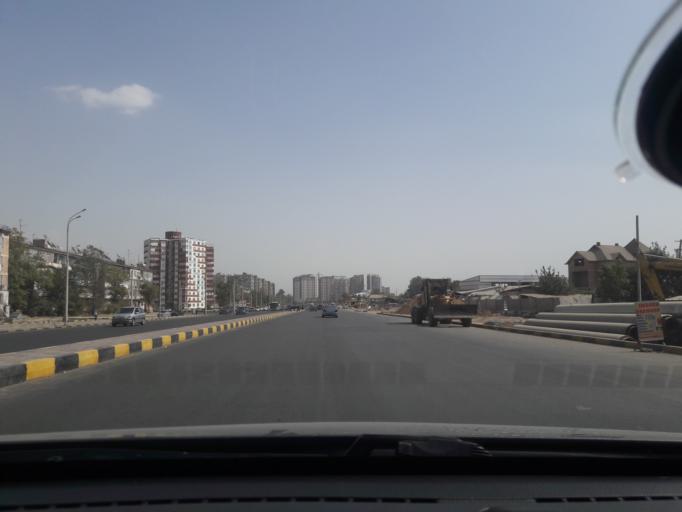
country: TJ
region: Dushanbe
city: Dushanbe
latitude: 38.5584
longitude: 68.7523
